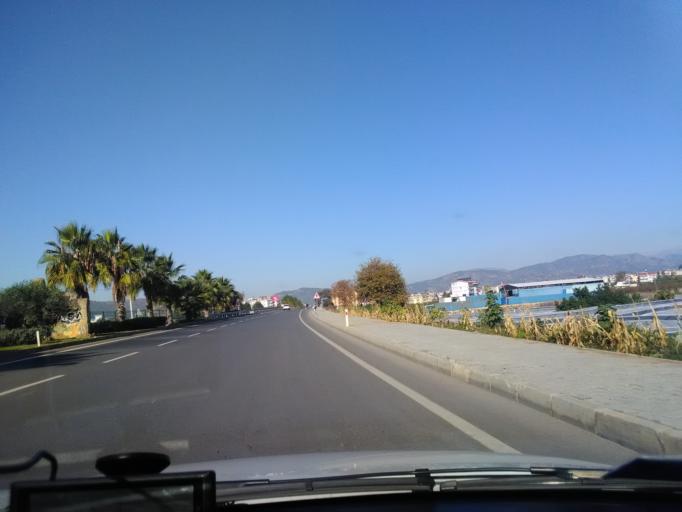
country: TR
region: Antalya
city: Gazipasa
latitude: 36.2590
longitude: 32.3243
